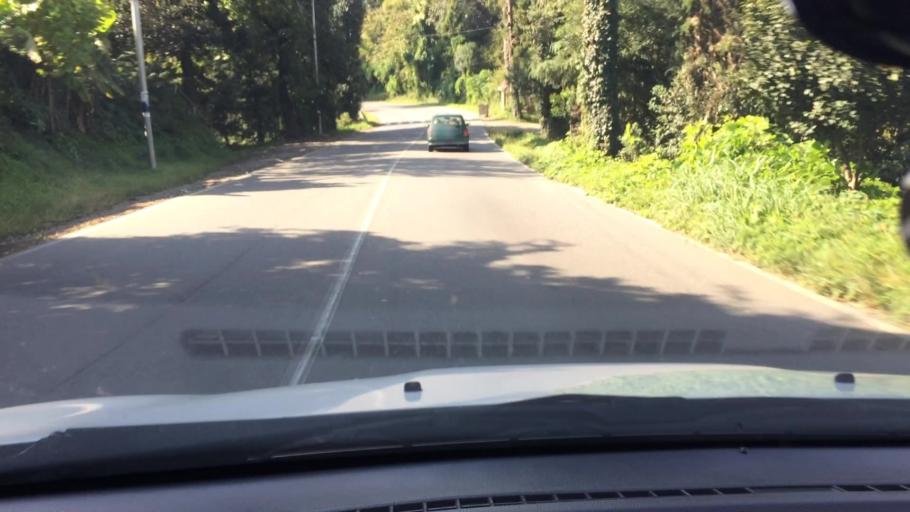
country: GE
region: Ajaria
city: Kobuleti
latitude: 41.7524
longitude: 41.7460
